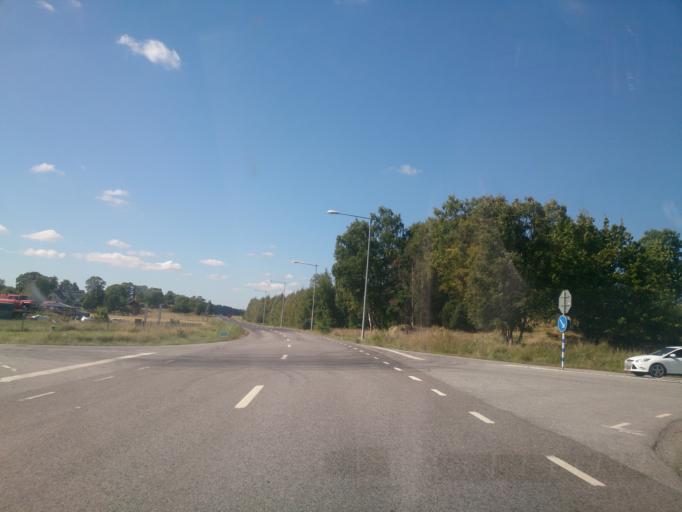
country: SE
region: OEstergoetland
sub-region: Norrkopings Kommun
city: Krokek
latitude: 58.5820
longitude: 16.5570
